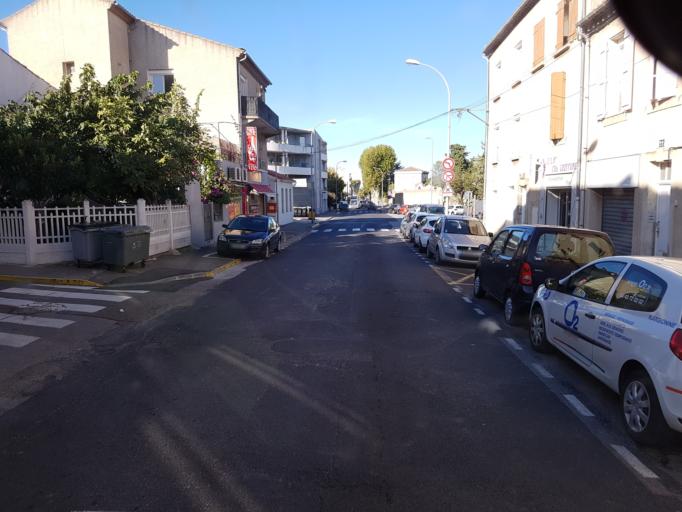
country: FR
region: Languedoc-Roussillon
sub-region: Departement de l'Aude
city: Narbonne
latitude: 43.1898
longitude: 3.0091
